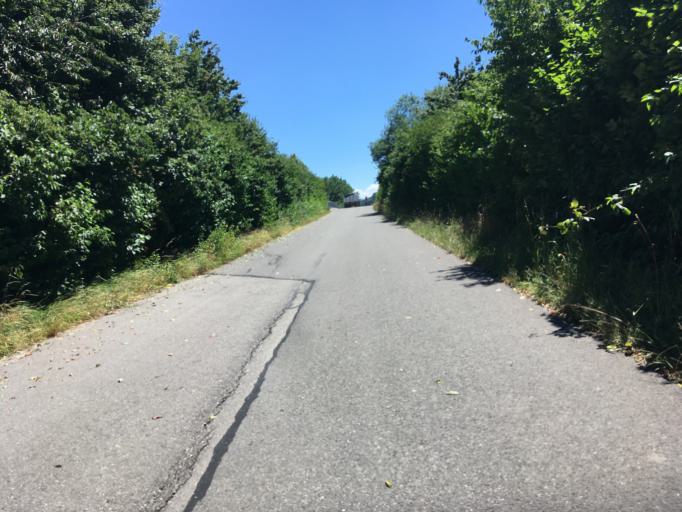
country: CH
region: Vaud
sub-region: Broye-Vully District
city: Avenches
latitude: 46.8922
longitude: 7.0407
